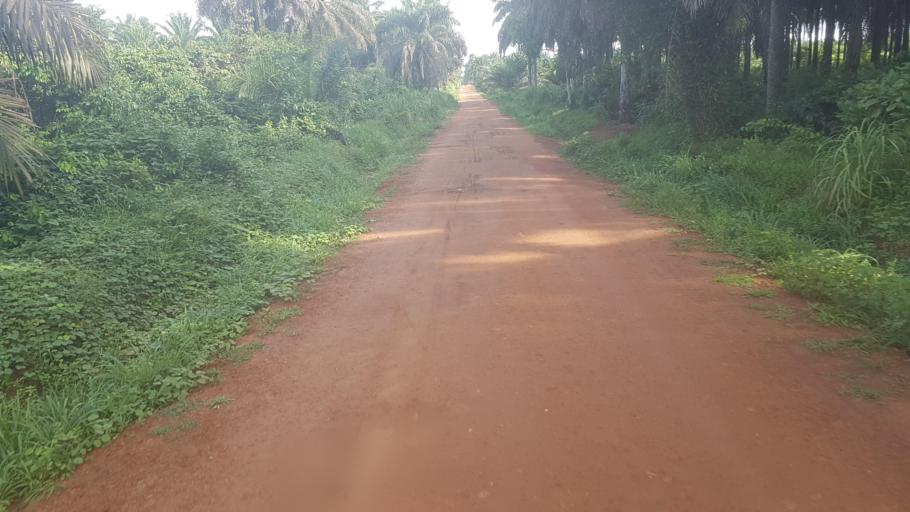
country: SL
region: Southern Province
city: Sumbuya
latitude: 7.6112
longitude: -12.1428
